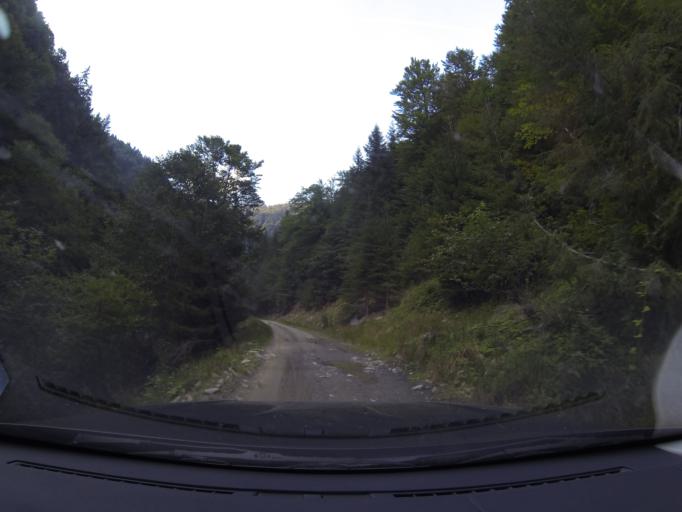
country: RO
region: Arges
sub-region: Comuna Arefu
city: Arefu
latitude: 45.5116
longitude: 24.6686
